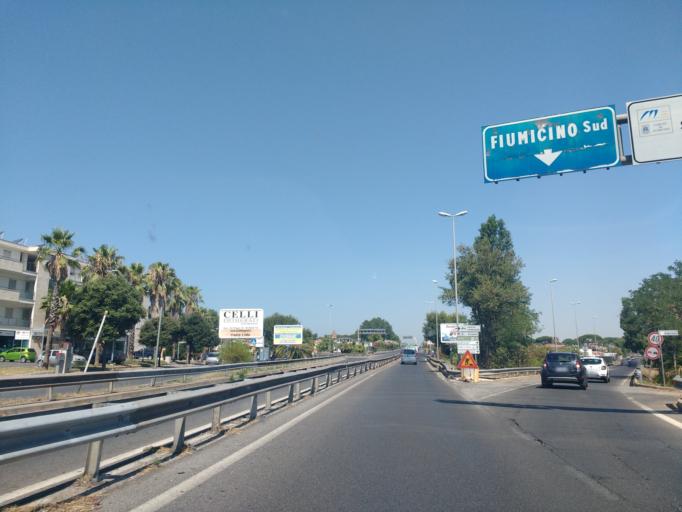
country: IT
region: Latium
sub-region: Citta metropolitana di Roma Capitale
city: Fiumicino-Isola Sacra
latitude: 41.7688
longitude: 12.2602
